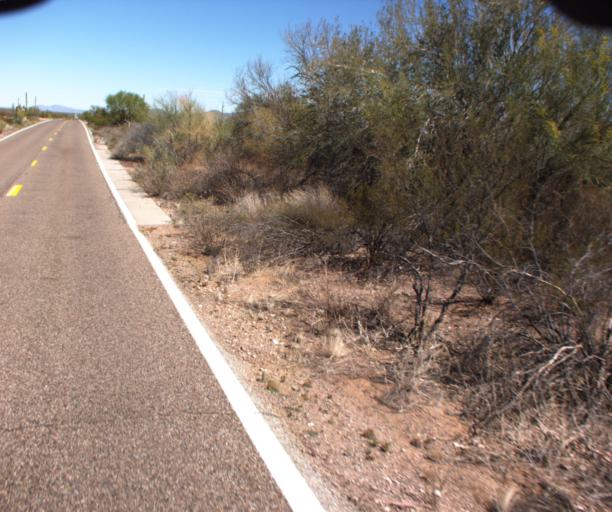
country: MX
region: Sonora
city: Sonoyta
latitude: 32.1109
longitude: -112.7699
